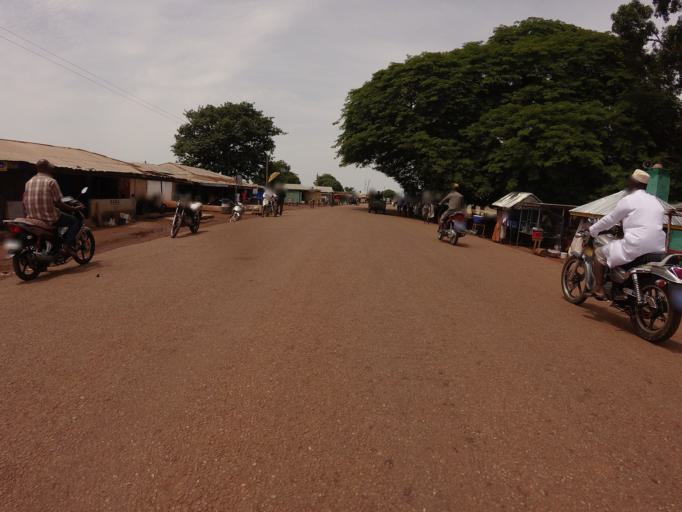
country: GH
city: Kpandae
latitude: 8.8580
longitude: 0.0563
